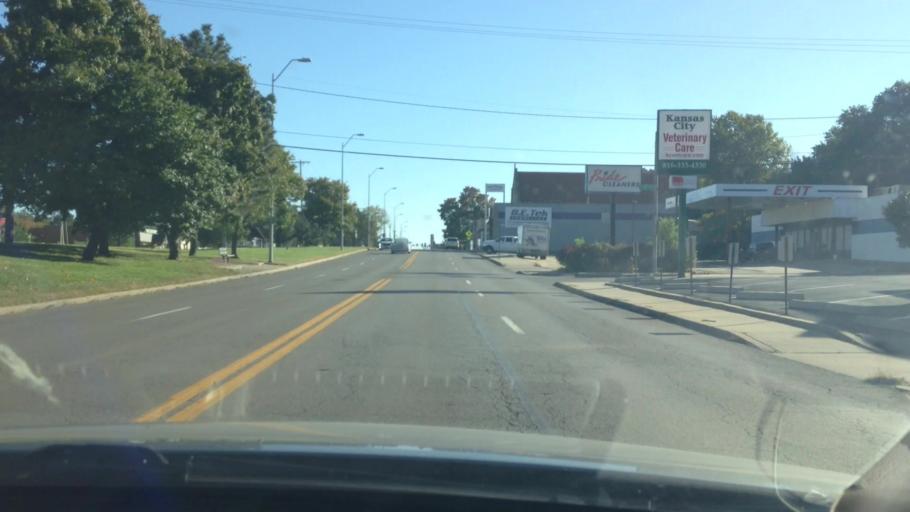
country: US
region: Kansas
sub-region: Johnson County
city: Mission Hills
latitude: 38.9964
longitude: -94.5941
